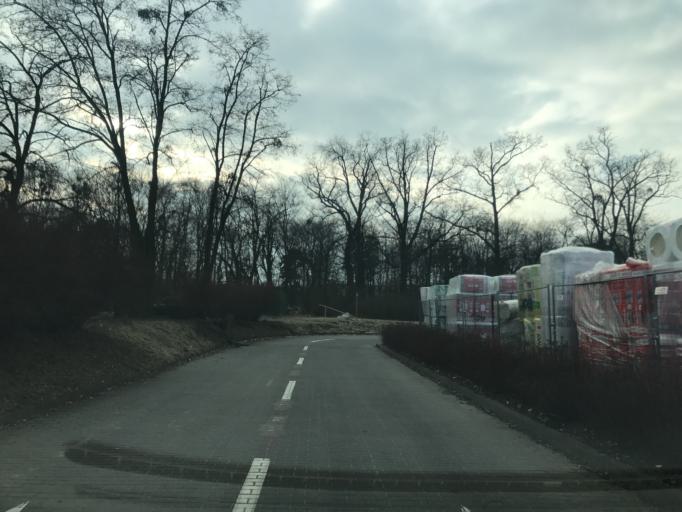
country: PL
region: Kujawsko-Pomorskie
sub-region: Powiat torunski
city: Lubicz Dolny
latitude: 53.0314
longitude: 18.6923
